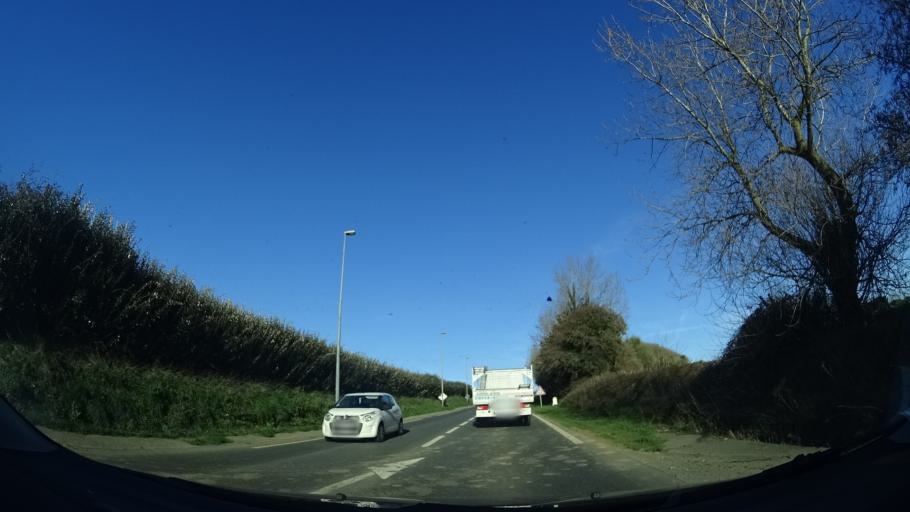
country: FR
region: Brittany
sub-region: Departement du Finistere
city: Saint-Pol-de-Leon
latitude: 48.6864
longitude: -4.0001
